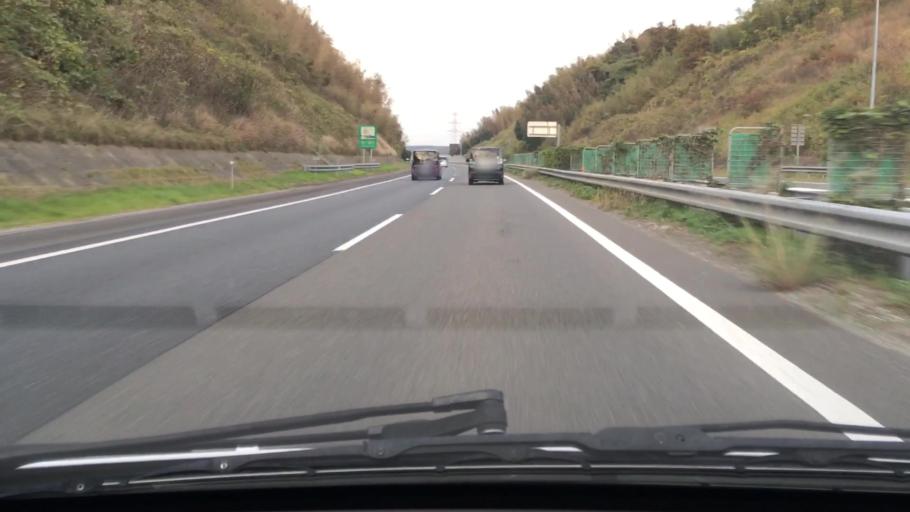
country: JP
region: Chiba
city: Kisarazu
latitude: 35.3871
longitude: 139.9991
